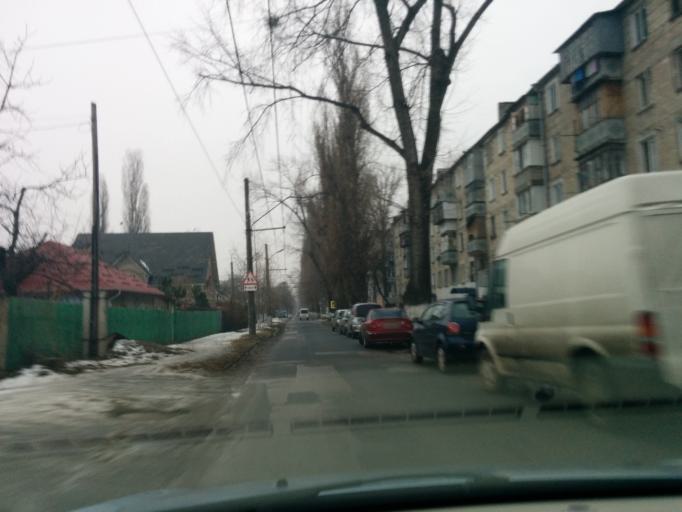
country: MD
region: Chisinau
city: Chisinau
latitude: 46.9994
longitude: 28.8624
